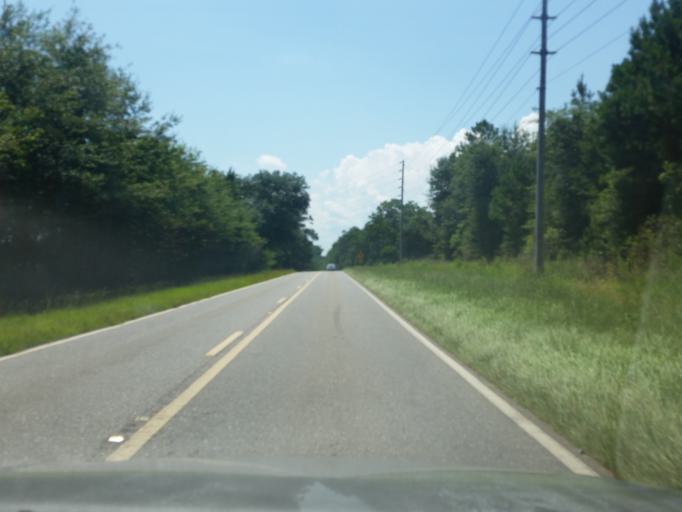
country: US
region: Alabama
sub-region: Baldwin County
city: Robertsdale
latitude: 30.6260
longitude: -87.6602
